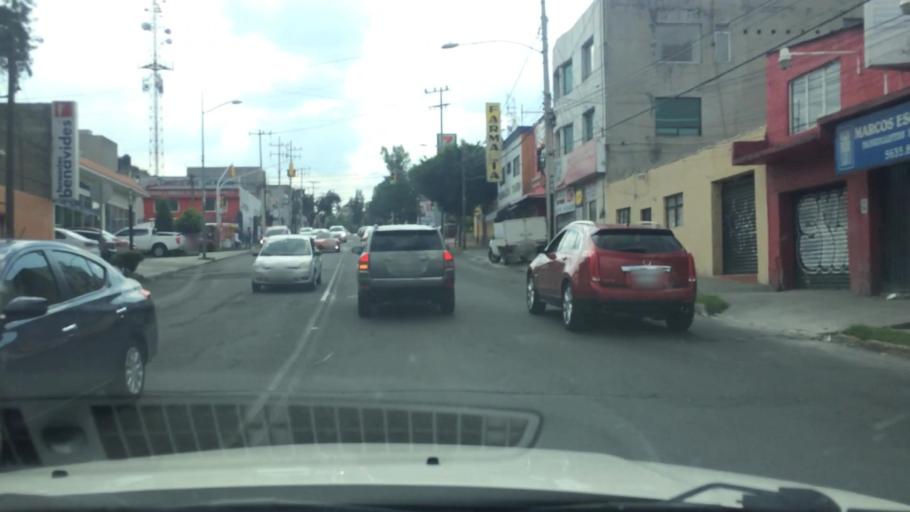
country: MX
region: Mexico City
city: Magdalena Contreras
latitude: 19.3487
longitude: -99.2295
